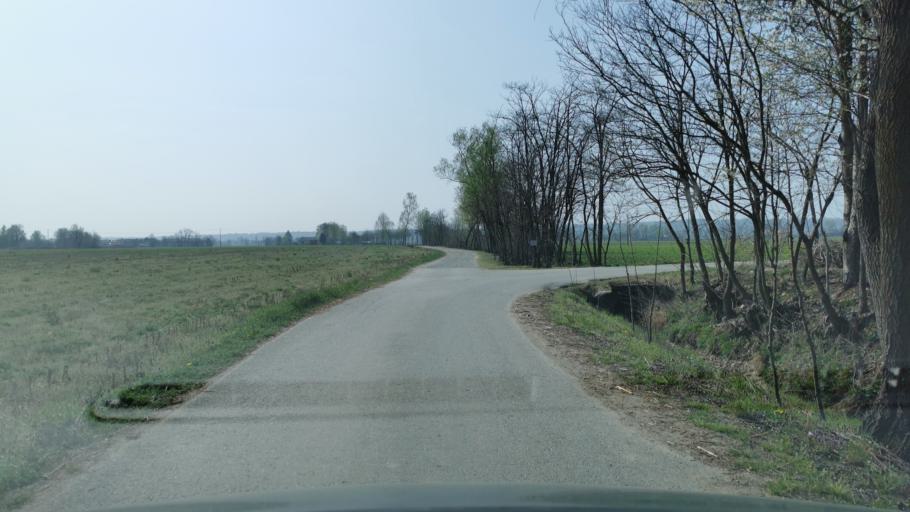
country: IT
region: Piedmont
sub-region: Provincia di Torino
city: Favria
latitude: 45.2976
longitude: 7.6947
